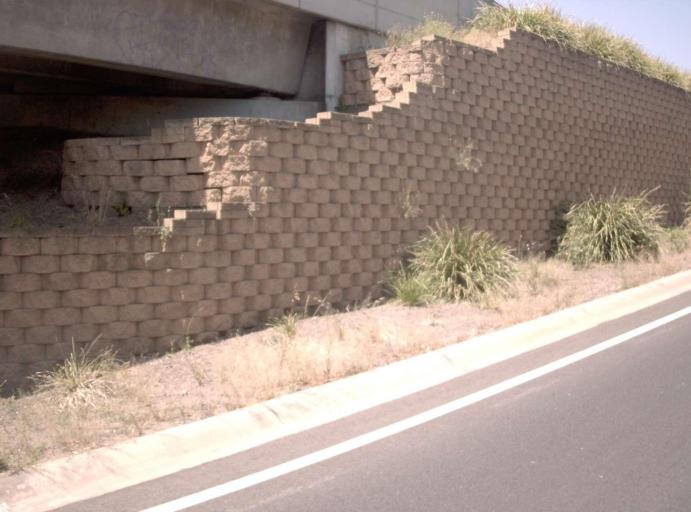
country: AU
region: Victoria
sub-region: Moreland
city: Pascoe Vale
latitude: -37.7335
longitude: 144.9249
